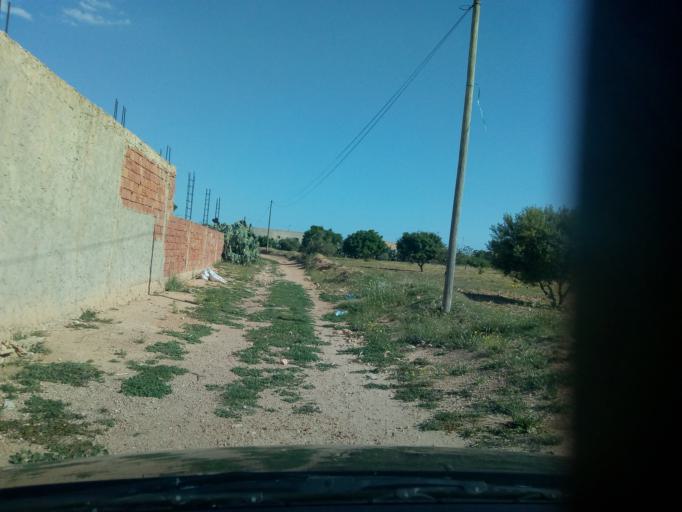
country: TN
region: Safaqis
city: Sfax
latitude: 34.7274
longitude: 10.6010
